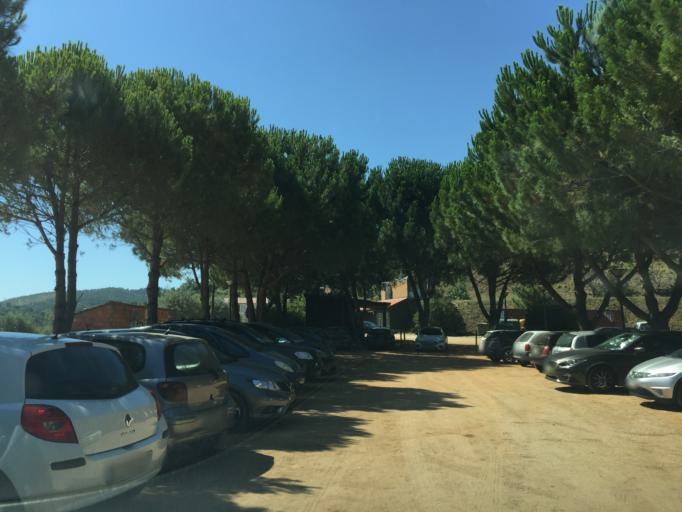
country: PT
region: Santarem
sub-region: Constancia
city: Constancia
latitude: 39.5451
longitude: -8.2772
